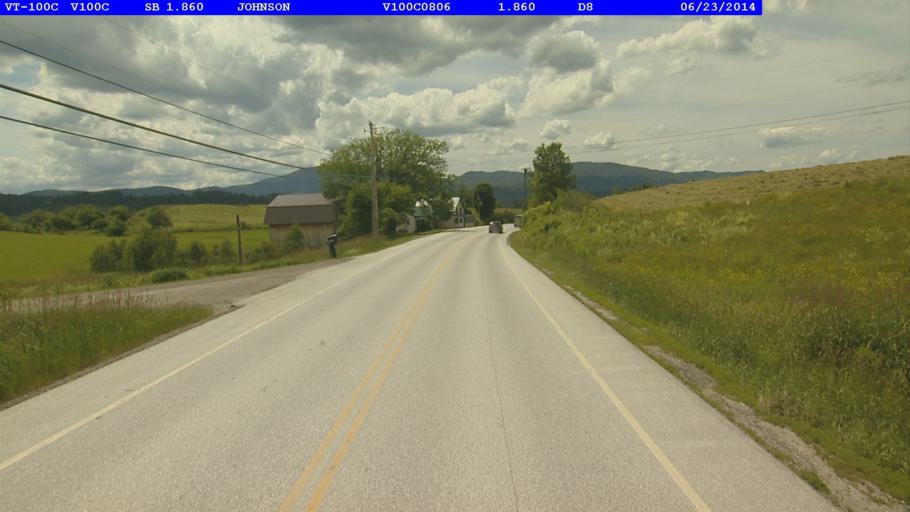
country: US
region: Vermont
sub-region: Lamoille County
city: Johnson
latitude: 44.6451
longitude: -72.6455
